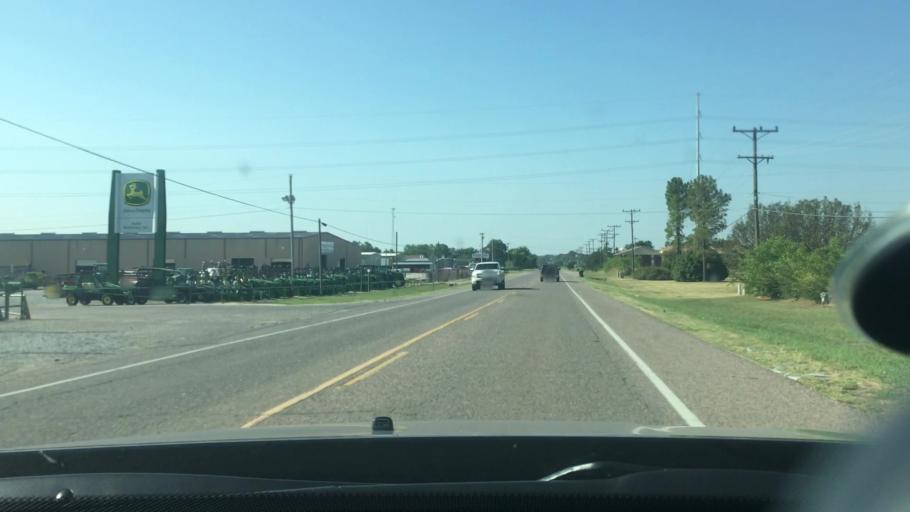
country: US
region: Oklahoma
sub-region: Bryan County
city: Durant
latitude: 34.0245
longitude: -96.3729
